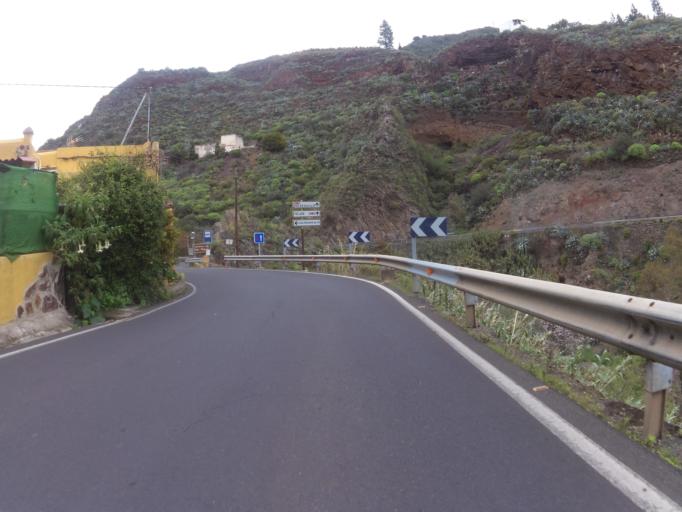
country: ES
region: Canary Islands
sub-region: Provincia de Las Palmas
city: Valsequillo de Gran Canaria
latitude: 27.9910
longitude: -15.5025
